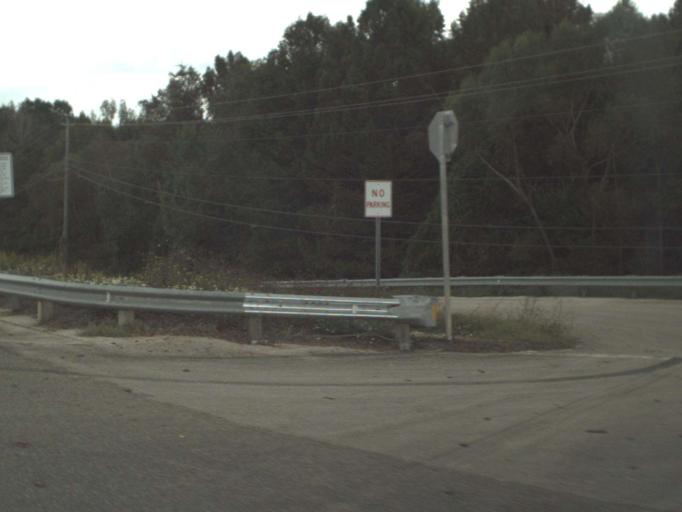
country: US
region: Florida
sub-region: Liberty County
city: Bristol
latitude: 30.4326
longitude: -84.9964
